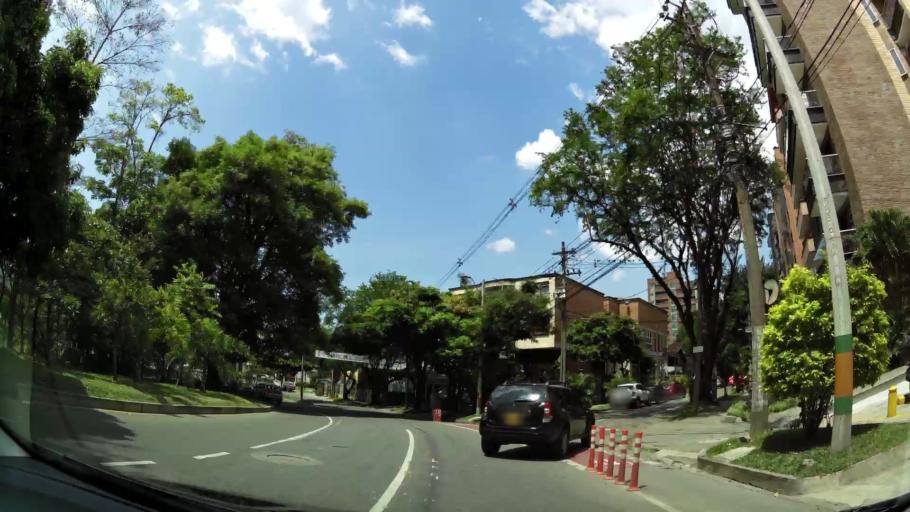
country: CO
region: Antioquia
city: Envigado
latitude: 6.1849
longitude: -75.5825
